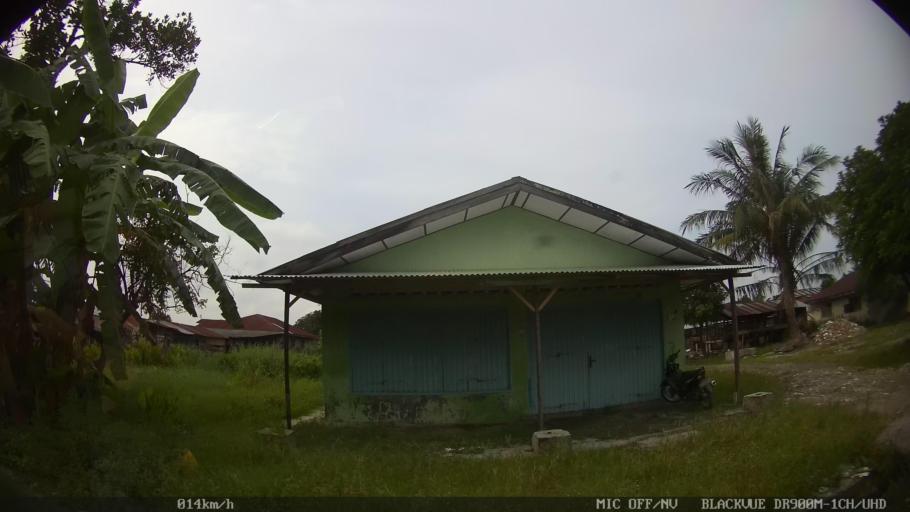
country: ID
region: North Sumatra
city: Medan
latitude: 3.5695
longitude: 98.7523
